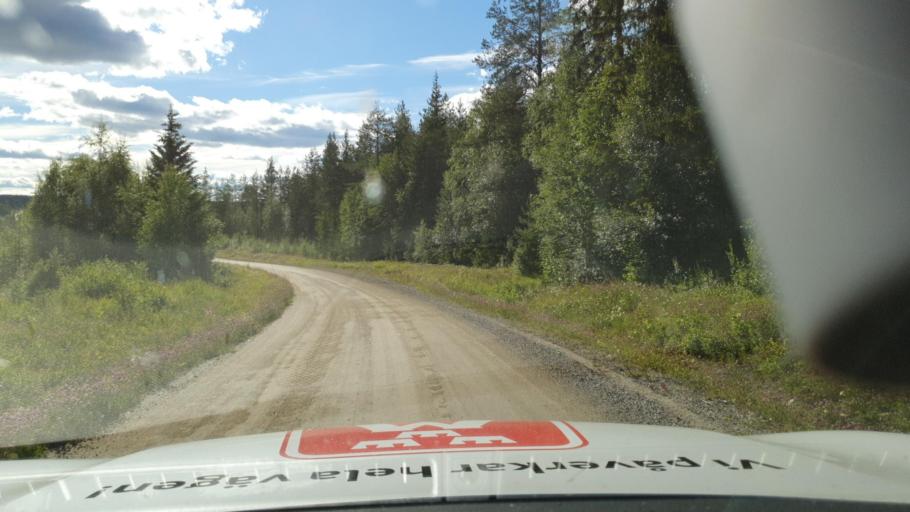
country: SE
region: Vaesterbotten
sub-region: Lycksele Kommun
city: Lycksele
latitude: 64.4108
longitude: 18.4955
